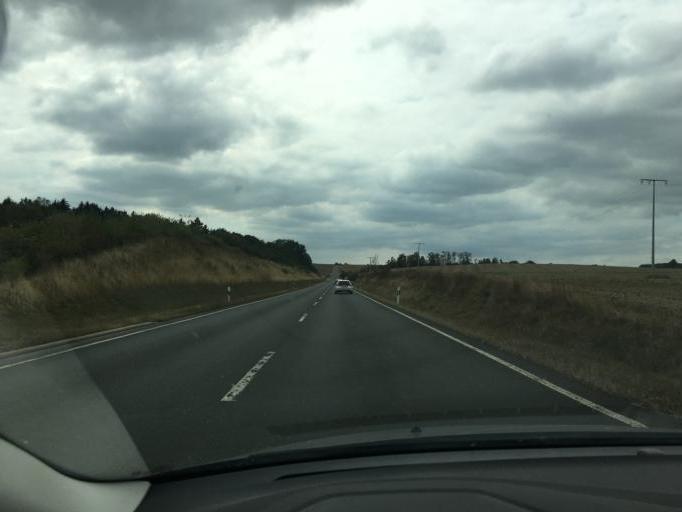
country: DE
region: Thuringia
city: Bad Lobenstein
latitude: 50.4898
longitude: 11.6534
